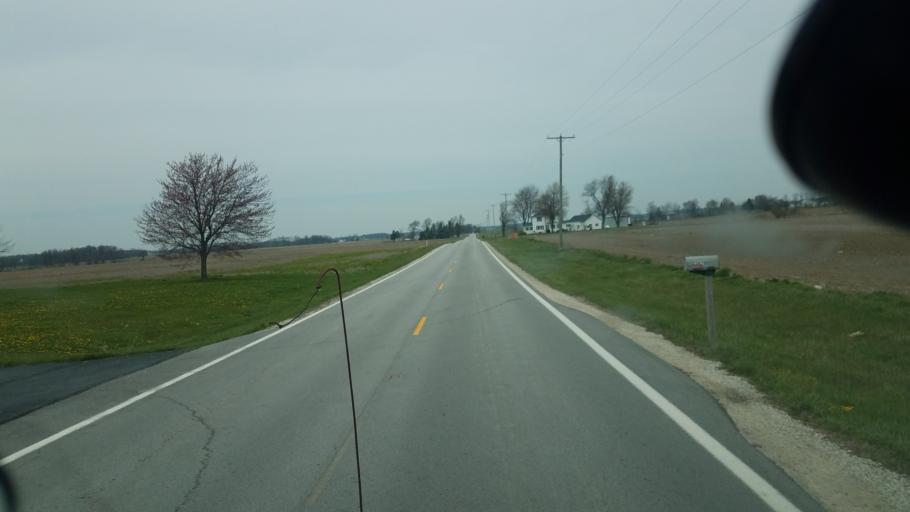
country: US
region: Ohio
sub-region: Wyandot County
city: Carey
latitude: 40.9794
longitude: -83.4765
